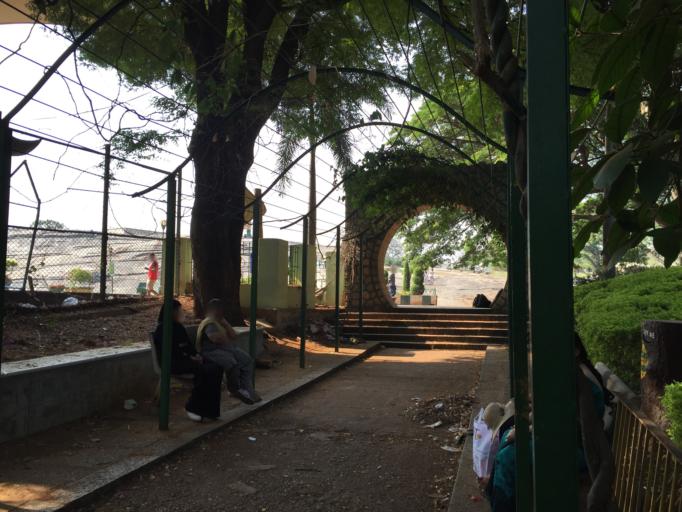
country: IN
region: Karnataka
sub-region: Bangalore Urban
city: Bangalore
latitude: 12.9495
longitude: 77.5887
